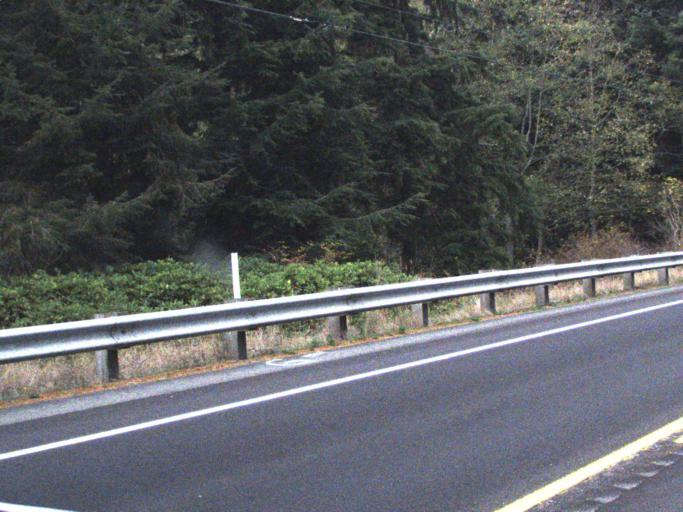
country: US
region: Washington
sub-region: Island County
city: Camano
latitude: 48.1188
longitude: -122.5871
